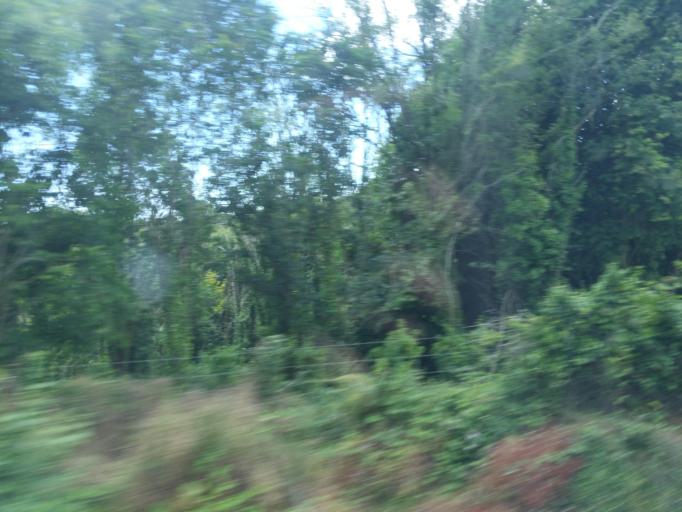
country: GB
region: England
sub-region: Cornwall
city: Saltash
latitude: 50.3942
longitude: -4.2527
